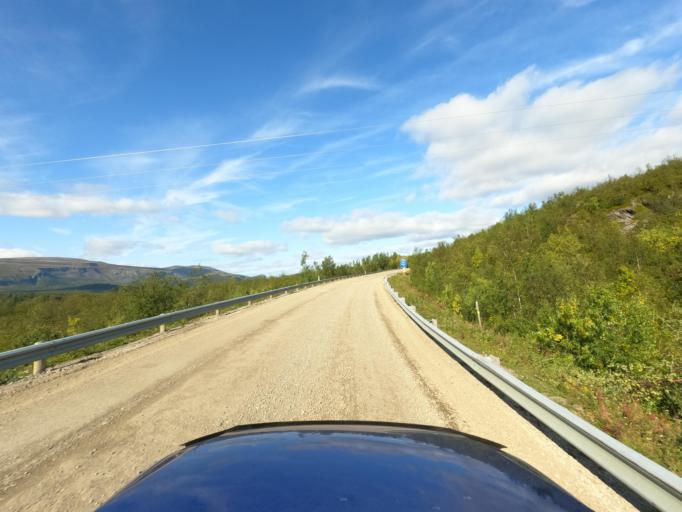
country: NO
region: Finnmark Fylke
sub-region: Porsanger
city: Lakselv
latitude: 69.8803
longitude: 25.0223
